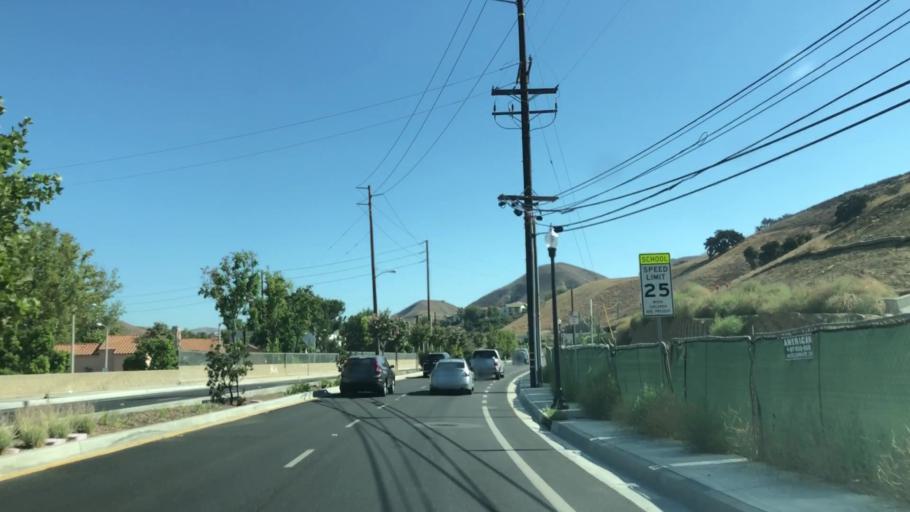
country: US
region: California
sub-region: Los Angeles County
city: Agoura
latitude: 34.1370
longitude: -118.7019
